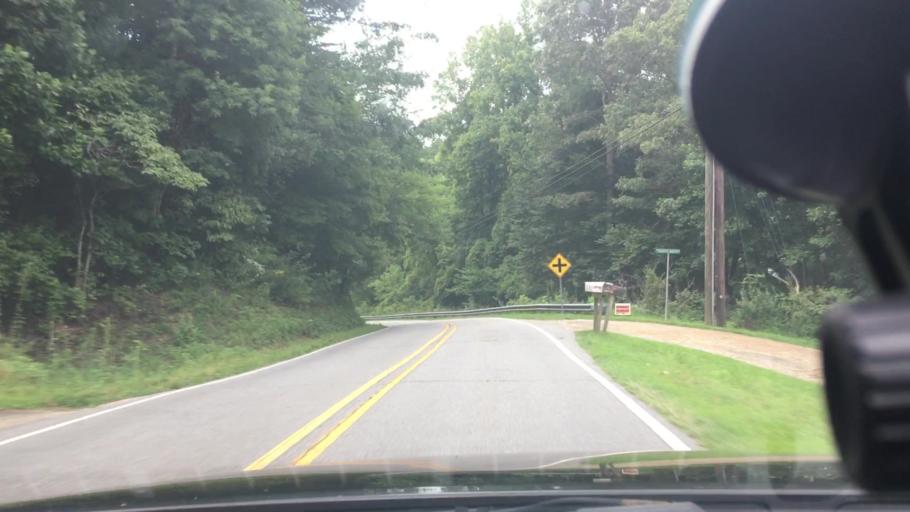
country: US
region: North Carolina
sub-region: McDowell County
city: West Marion
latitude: 35.6567
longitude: -82.0166
